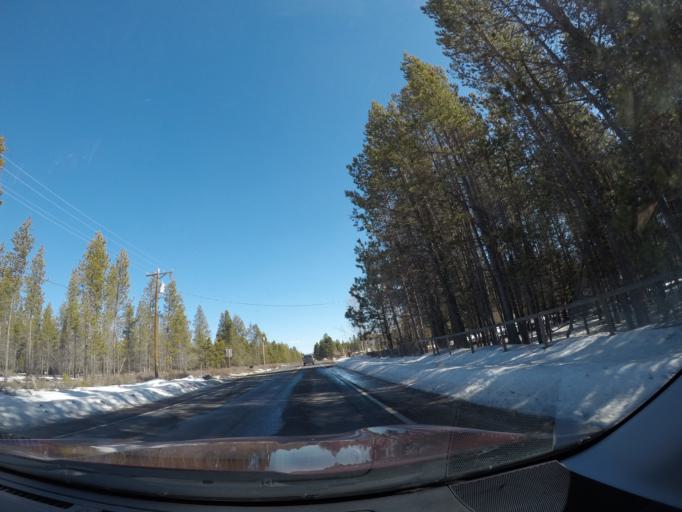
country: US
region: Oregon
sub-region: Deschutes County
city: Sunriver
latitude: 43.8630
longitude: -121.4671
